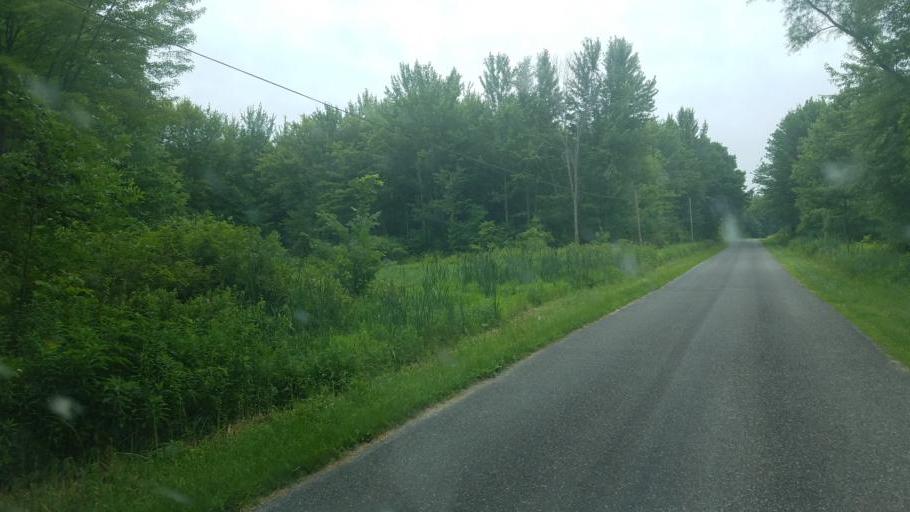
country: US
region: Ohio
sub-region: Ashtabula County
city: Orwell
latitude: 41.4578
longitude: -80.7621
